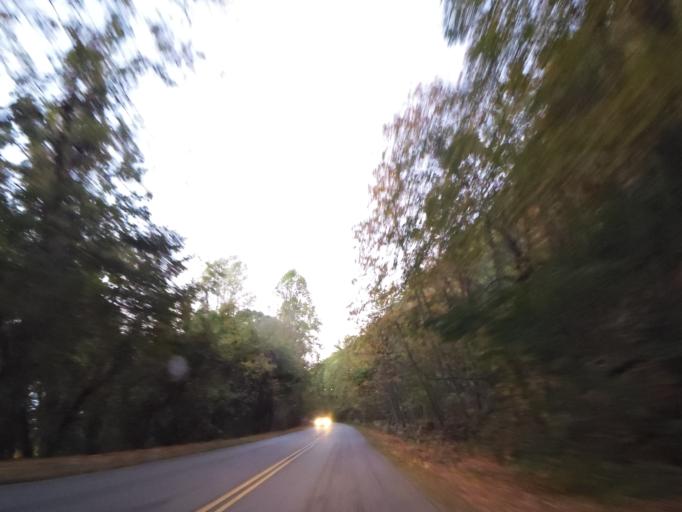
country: US
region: Tennessee
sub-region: Blount County
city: Wildwood
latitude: 35.6960
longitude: -83.8765
